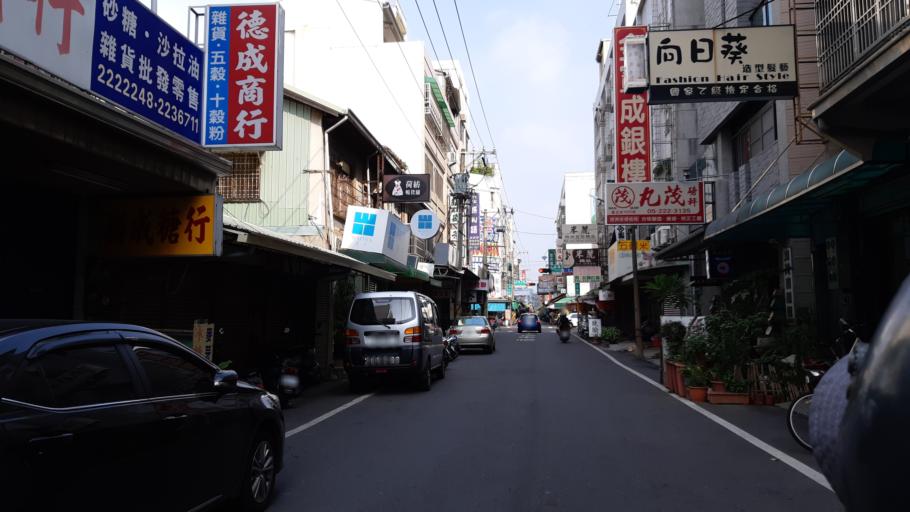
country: TW
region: Taiwan
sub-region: Chiayi
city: Jiayi Shi
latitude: 23.4792
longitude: 120.4524
